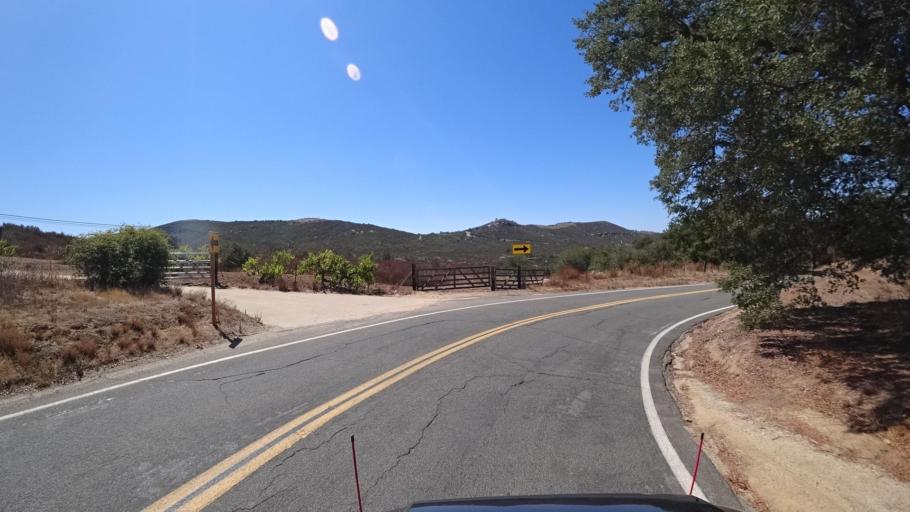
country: US
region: California
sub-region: San Diego County
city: San Diego Country Estates
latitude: 33.0535
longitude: -116.7769
